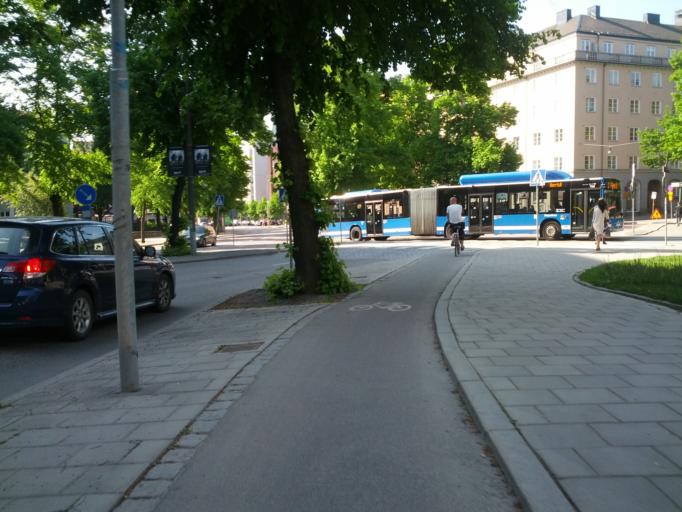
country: SE
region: Stockholm
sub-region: Stockholms Kommun
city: Stockholm
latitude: 59.3442
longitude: 18.0632
